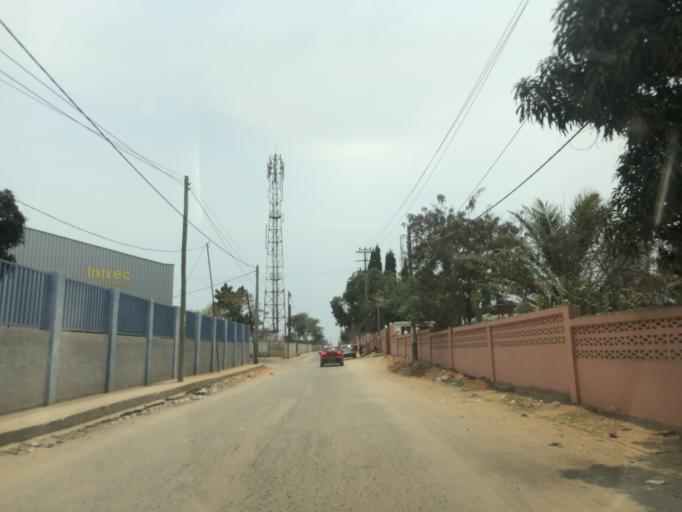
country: AO
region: Luanda
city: Luanda
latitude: -8.8893
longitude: 13.1968
